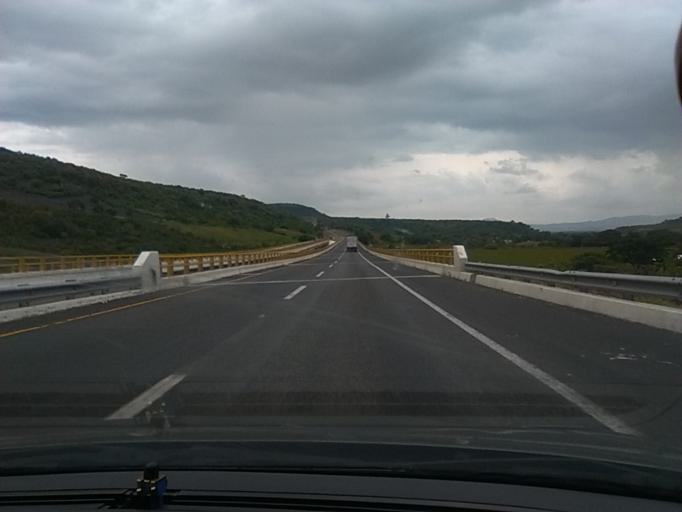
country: MX
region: Jalisco
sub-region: Zapotlan del Rey
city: Zapotlan del Rey
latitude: 20.4934
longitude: -102.9449
